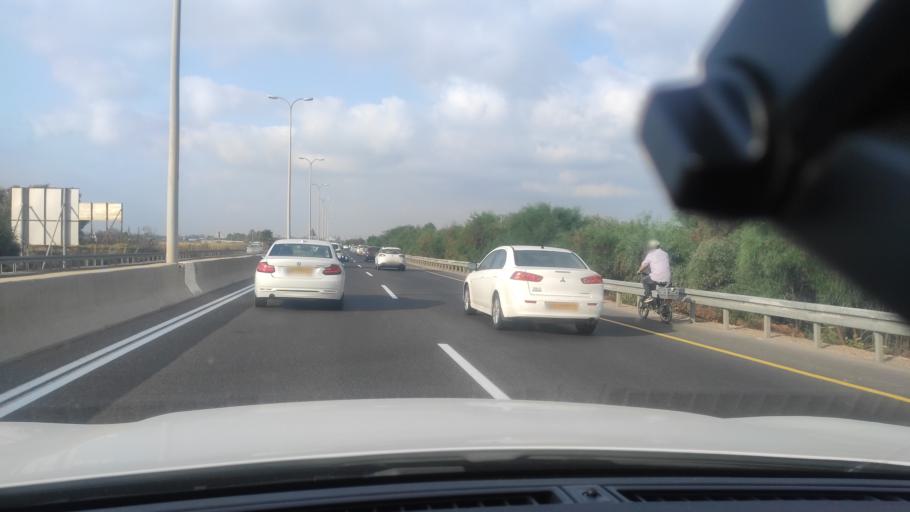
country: IL
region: Central District
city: Kfar Saba
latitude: 32.1498
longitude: 34.9202
